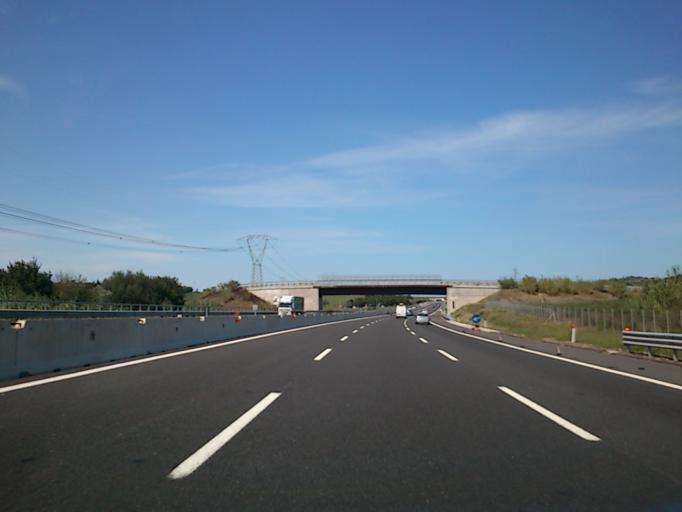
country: IT
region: The Marches
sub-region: Provincia di Pesaro e Urbino
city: Borgo Santa Maria
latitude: 43.9079
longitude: 12.8232
